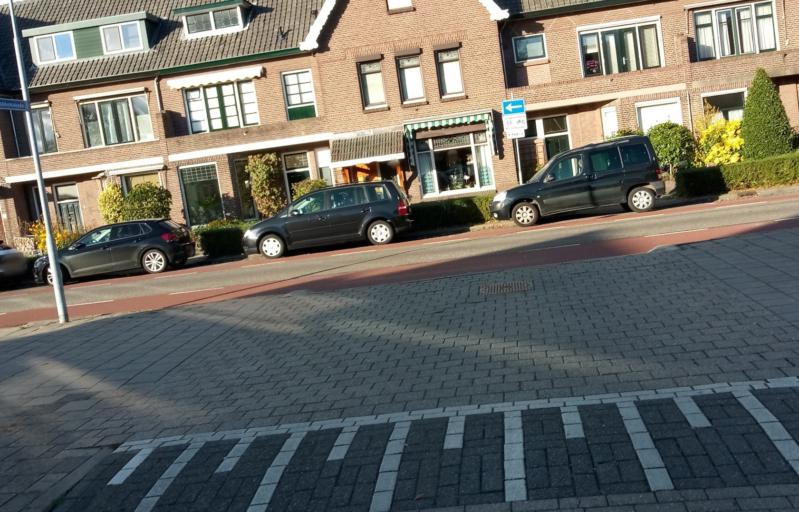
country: NL
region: Gelderland
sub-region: Gemeente Zutphen
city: Zutphen
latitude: 52.1413
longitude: 6.2061
